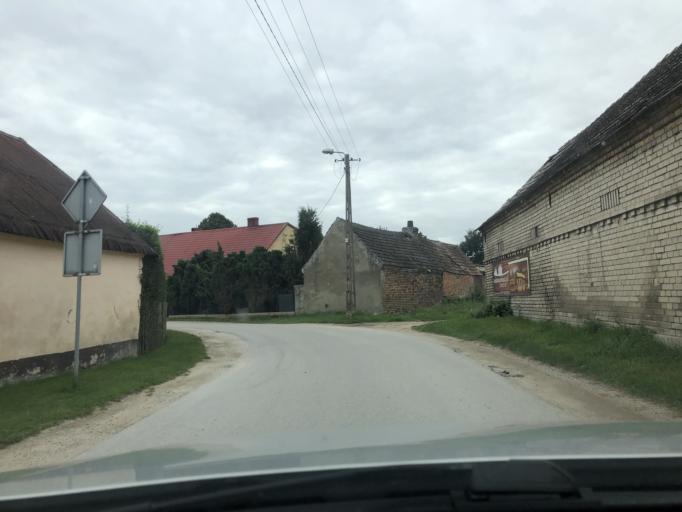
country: PL
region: Greater Poland Voivodeship
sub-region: Powiat pilski
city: Pila
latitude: 53.2652
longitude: 16.6937
